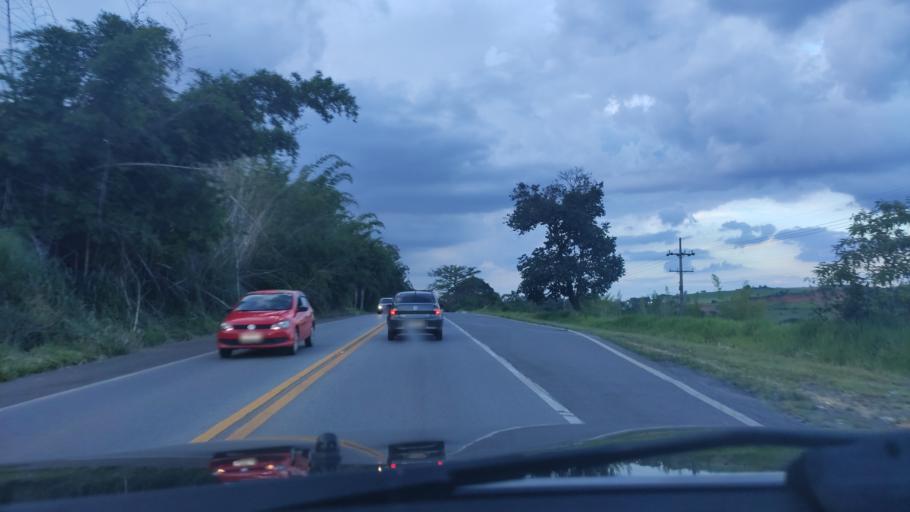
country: BR
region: Sao Paulo
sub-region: Braganca Paulista
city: Braganca Paulista
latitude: -22.8980
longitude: -46.5427
